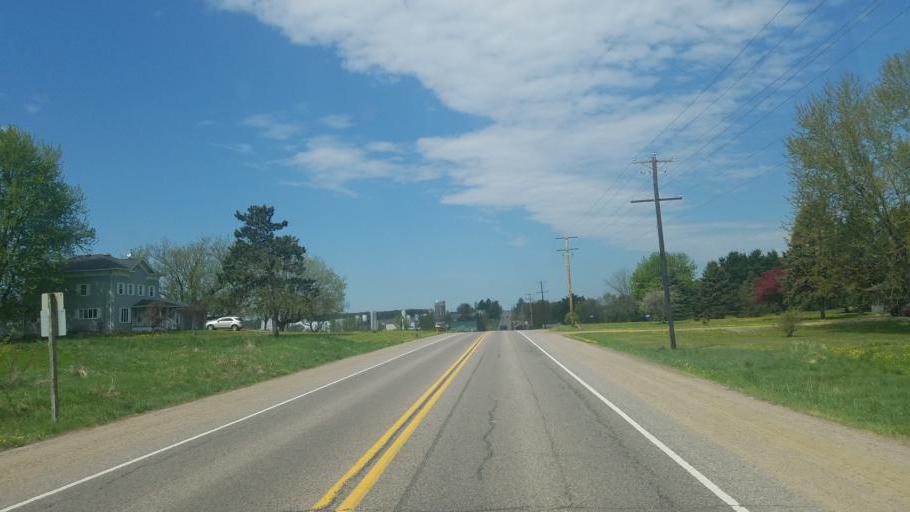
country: US
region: Wisconsin
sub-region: Clark County
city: Loyal
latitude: 44.5824
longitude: -90.3996
